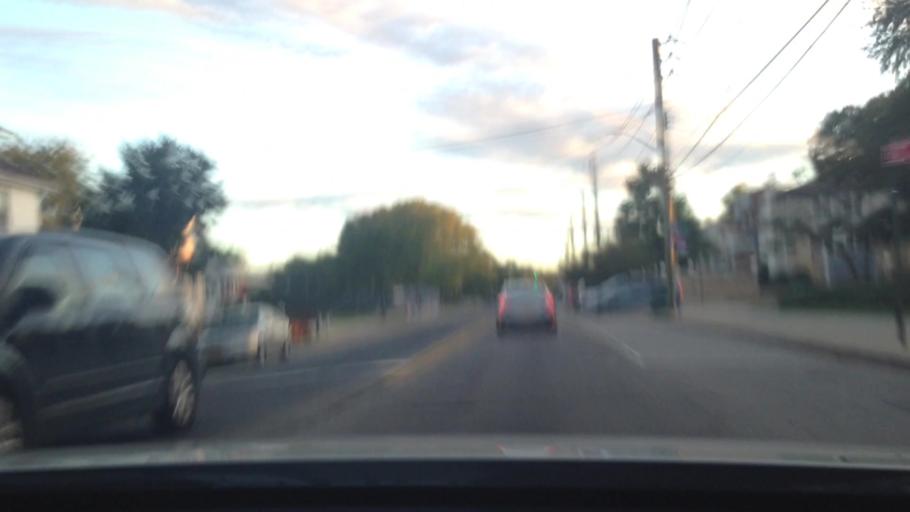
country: US
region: New York
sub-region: Nassau County
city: South Valley Stream
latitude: 40.6692
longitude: -73.7364
